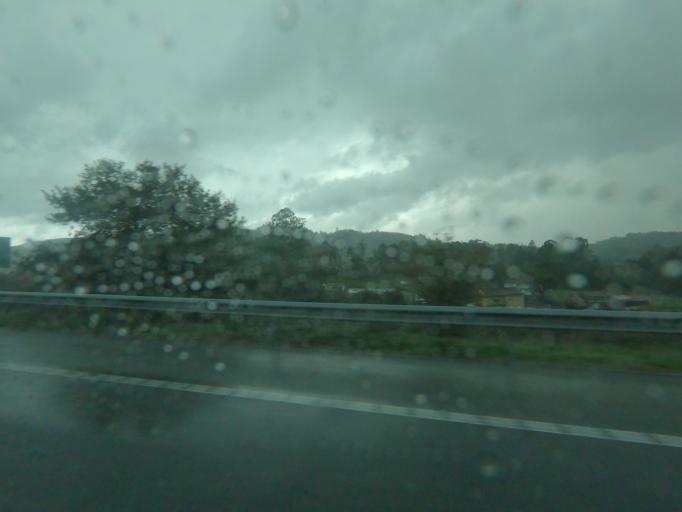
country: ES
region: Galicia
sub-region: Provincia de Pontevedra
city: Pontevedra
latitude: 42.3729
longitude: -8.6363
